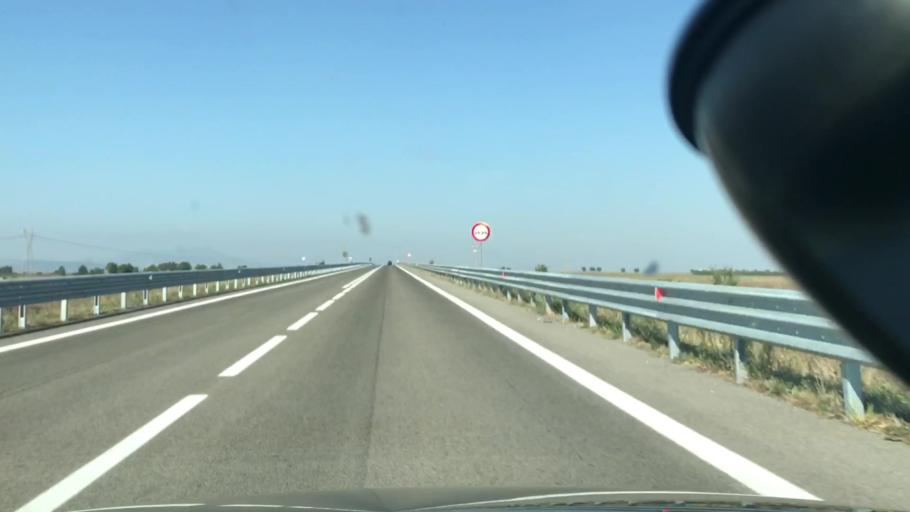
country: IT
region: Basilicate
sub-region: Provincia di Potenza
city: Palazzo San Gervasio
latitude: 40.9715
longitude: 15.9900
